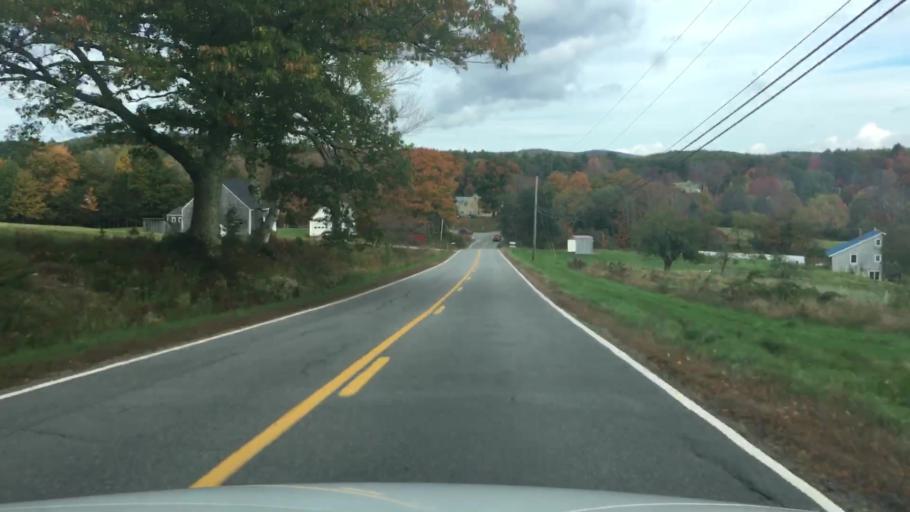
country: US
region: Maine
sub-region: Knox County
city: Hope
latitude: 44.2688
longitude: -69.1349
